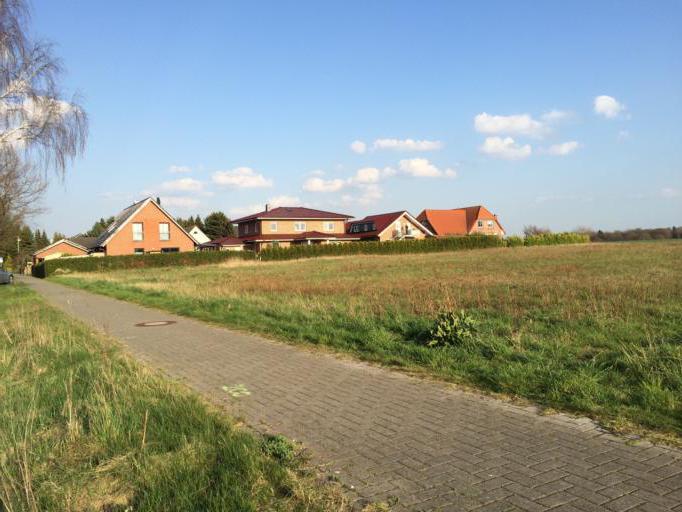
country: DE
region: Lower Saxony
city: Isernhagen Farster Bauerschaft
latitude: 52.4737
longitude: 9.8592
